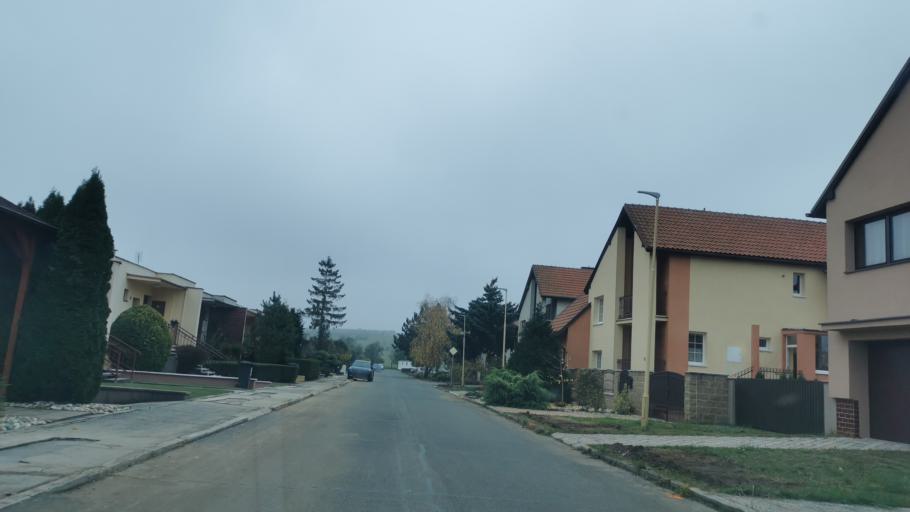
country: SK
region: Trnavsky
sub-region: Okres Skalica
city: Holic
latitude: 48.8126
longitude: 17.1707
